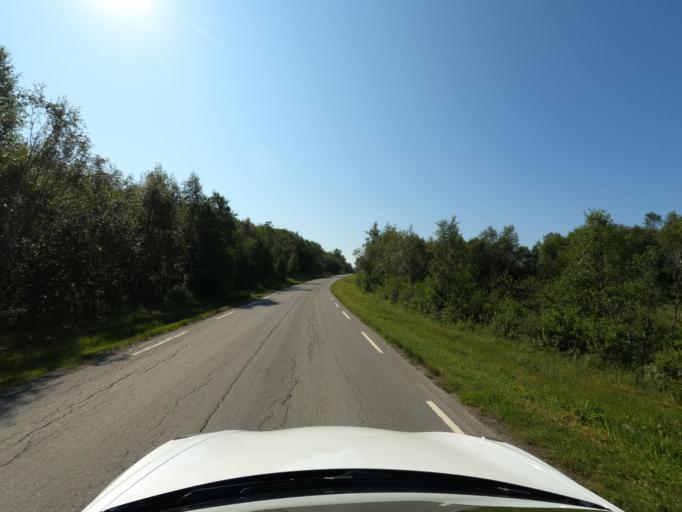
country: NO
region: Nordland
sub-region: Ballangen
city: Ballangen
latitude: 68.3612
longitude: 16.8786
